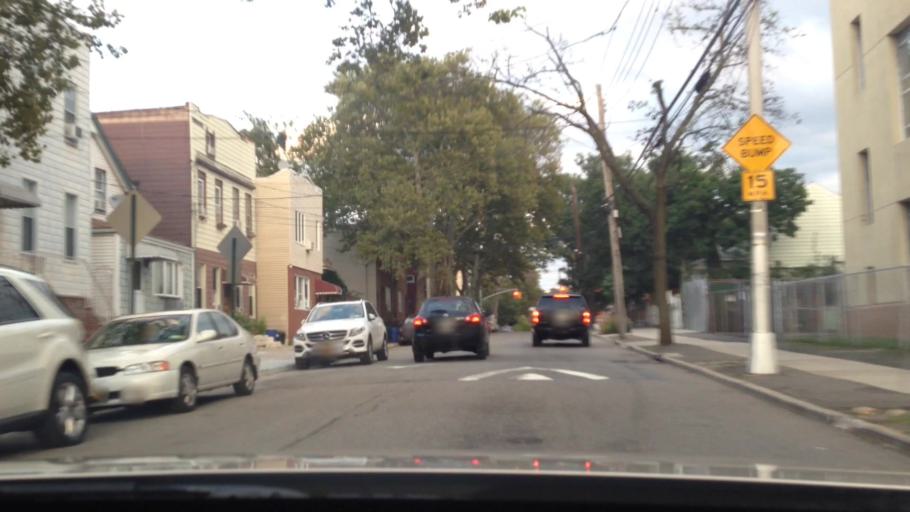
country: US
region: New York
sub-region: Queens County
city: Long Island City
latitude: 40.7231
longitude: -73.9061
